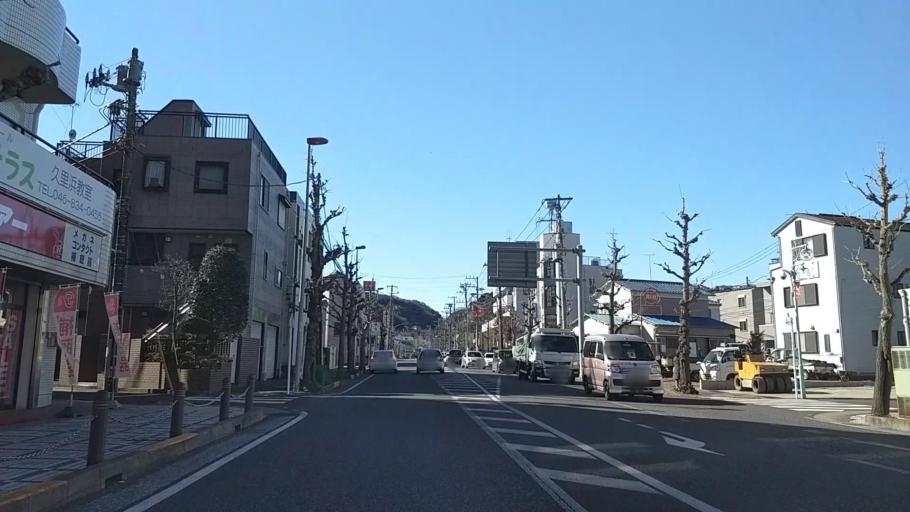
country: JP
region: Kanagawa
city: Yokosuka
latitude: 35.2286
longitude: 139.7027
